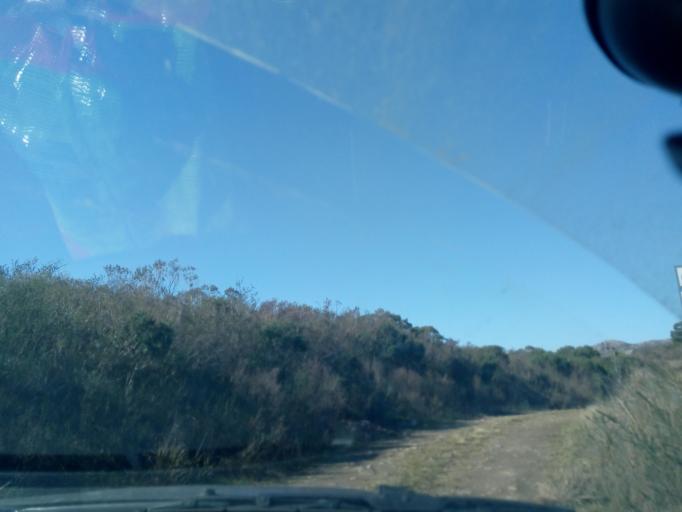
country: AR
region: Buenos Aires
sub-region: Partido de Tandil
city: Tandil
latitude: -37.3658
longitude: -59.1423
